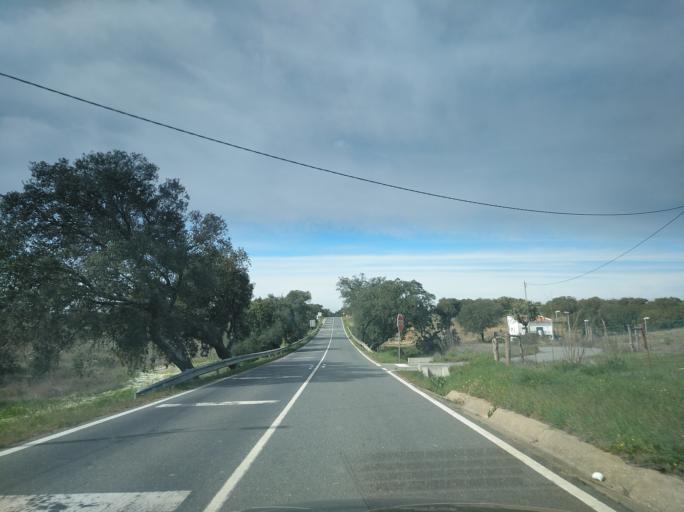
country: PT
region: Beja
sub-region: Mertola
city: Mertola
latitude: 37.7450
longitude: -7.7952
